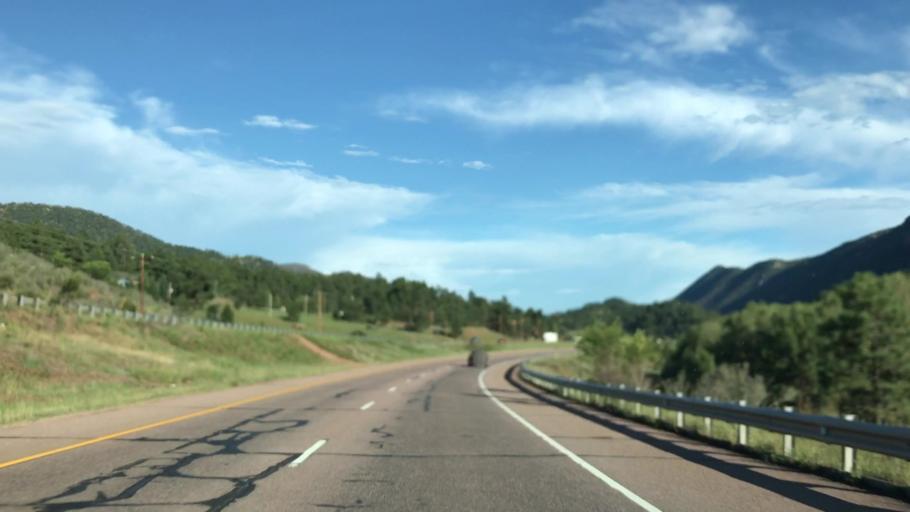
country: US
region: Colorado
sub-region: El Paso County
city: Cascade-Chipita Park
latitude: 38.9477
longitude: -105.0231
